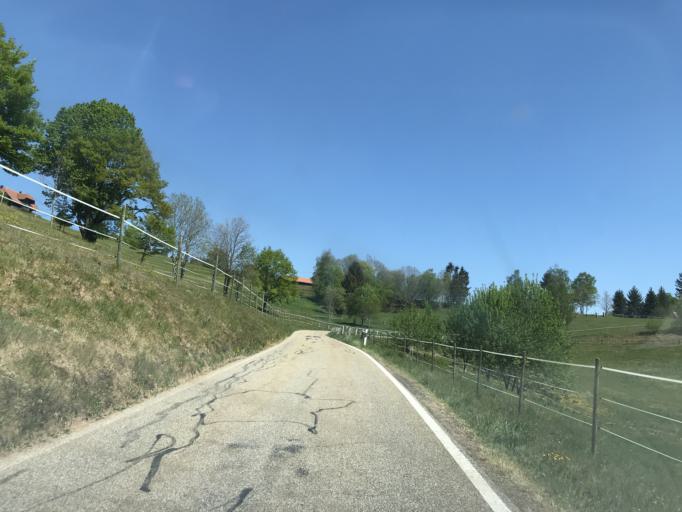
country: DE
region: Baden-Wuerttemberg
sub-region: Freiburg Region
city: Hasel
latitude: 47.6792
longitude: 7.8805
